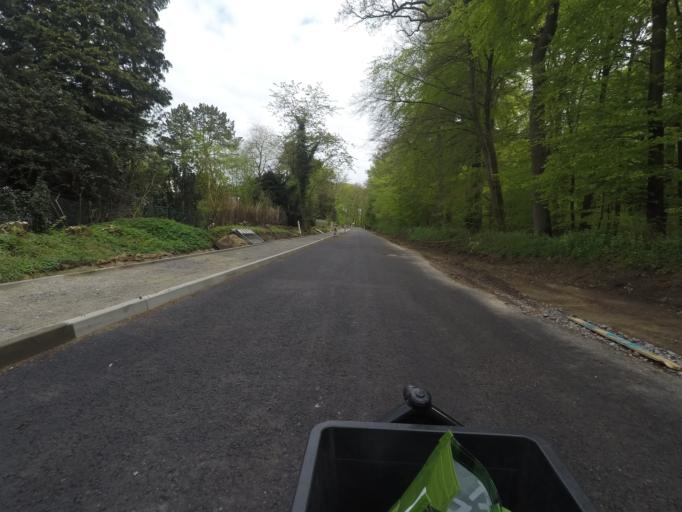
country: DE
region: Hamburg
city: Bergstedt
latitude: 53.6409
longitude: 10.1726
